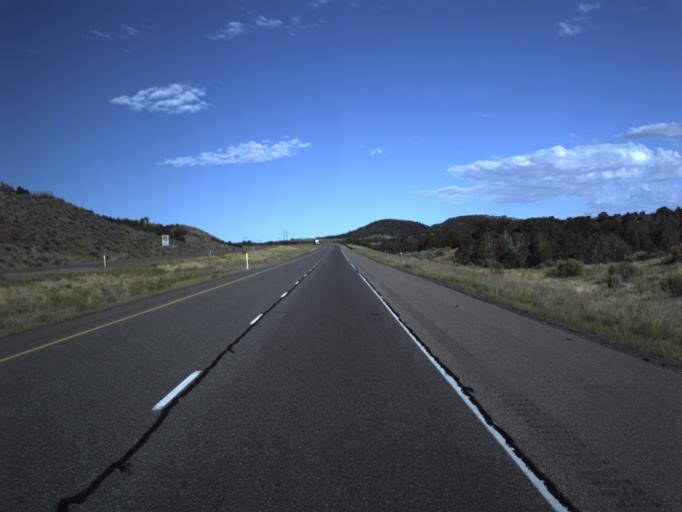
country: US
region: Utah
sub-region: Sevier County
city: Monroe
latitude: 38.5490
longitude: -112.3832
